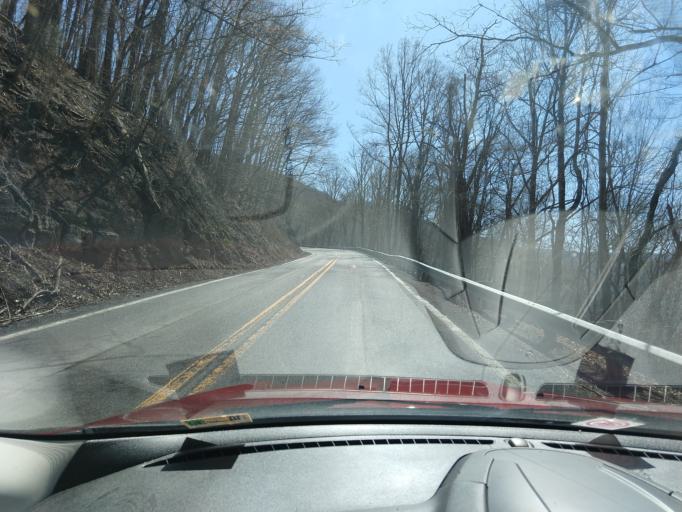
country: US
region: West Virginia
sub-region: Summers County
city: Hinton
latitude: 37.7640
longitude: -80.8913
